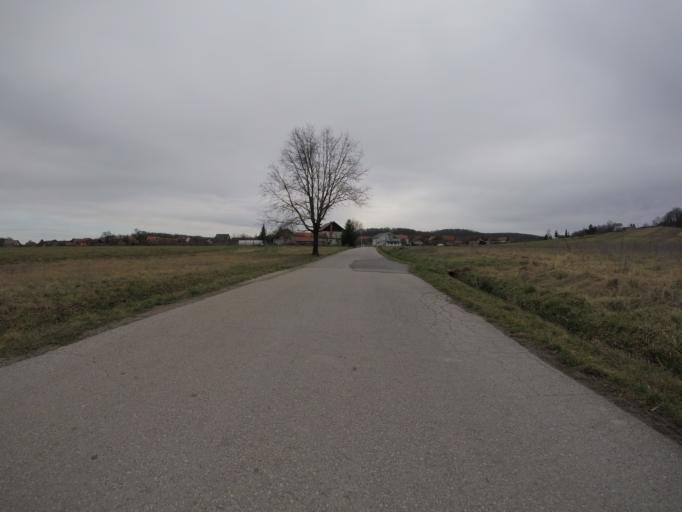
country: HR
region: Grad Zagreb
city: Strmec
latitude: 45.6665
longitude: 15.9200
